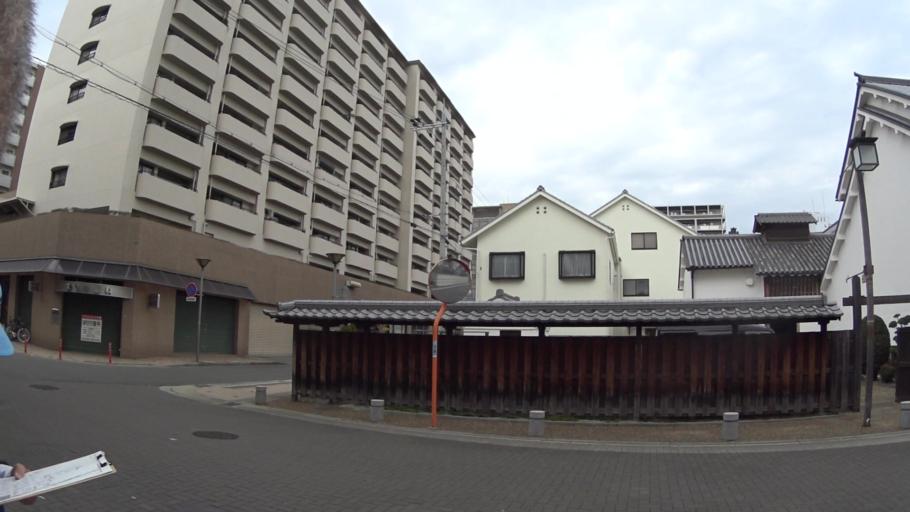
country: JP
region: Hyogo
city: Itami
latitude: 34.7825
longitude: 135.4161
